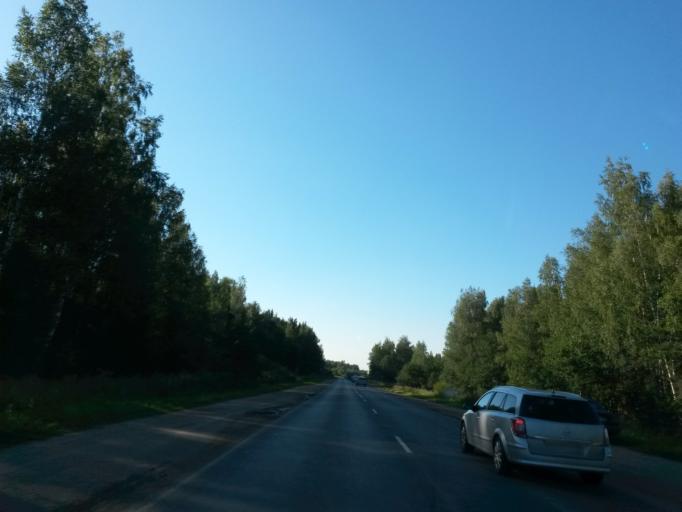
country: RU
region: Ivanovo
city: Novo-Talitsy
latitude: 57.0287
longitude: 40.7551
